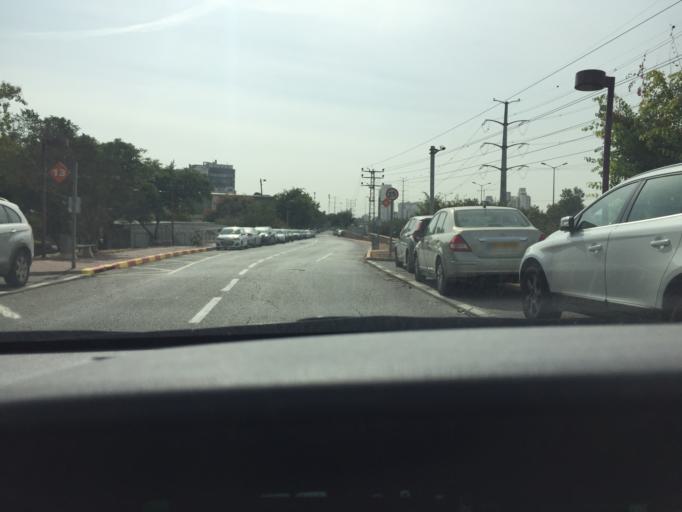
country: IL
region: Tel Aviv
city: Giv`at Shemu'el
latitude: 32.0714
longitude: 34.8432
